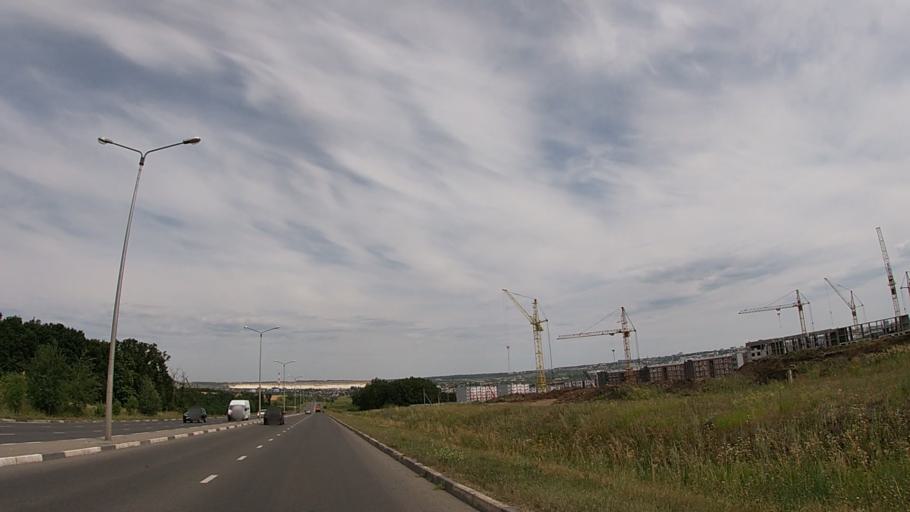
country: RU
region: Belgorod
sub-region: Belgorodskiy Rayon
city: Belgorod
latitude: 50.5953
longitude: 36.5308
